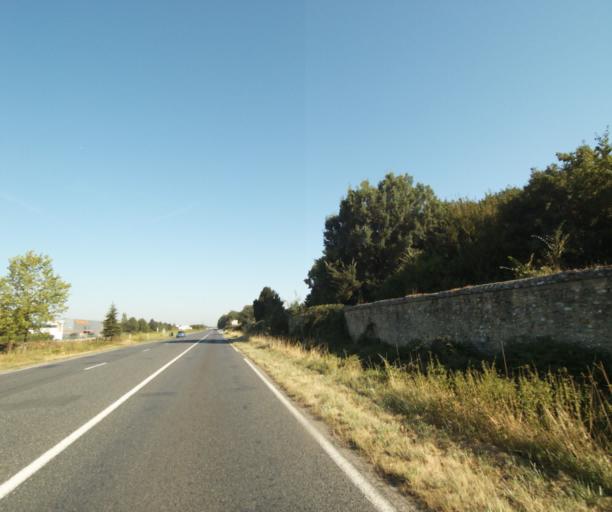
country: FR
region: Ile-de-France
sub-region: Departement de Seine-et-Marne
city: Savigny-le-Temple
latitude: 48.5924
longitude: 2.5980
